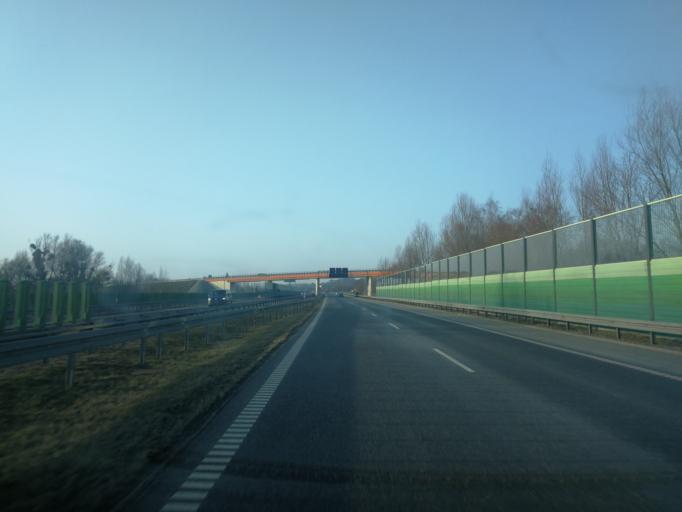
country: PL
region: Warmian-Masurian Voivodeship
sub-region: Powiat elblaski
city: Gronowo Gorne
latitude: 54.1308
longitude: 19.4583
